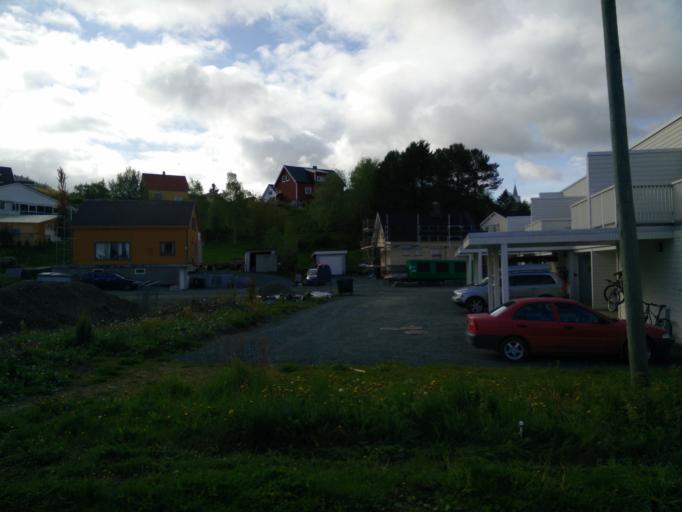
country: NO
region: Sor-Trondelag
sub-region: Melhus
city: Melhus
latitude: 63.3126
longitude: 10.1845
